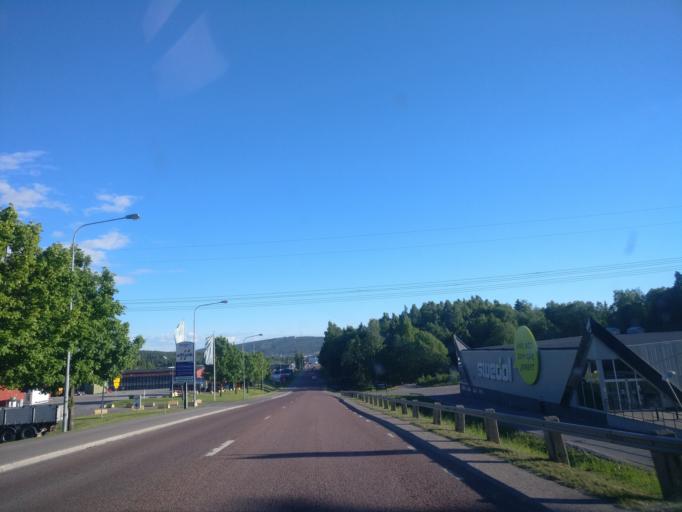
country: SE
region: Vaesternorrland
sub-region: Sundsvalls Kommun
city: Johannedal
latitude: 62.4228
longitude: 17.3456
